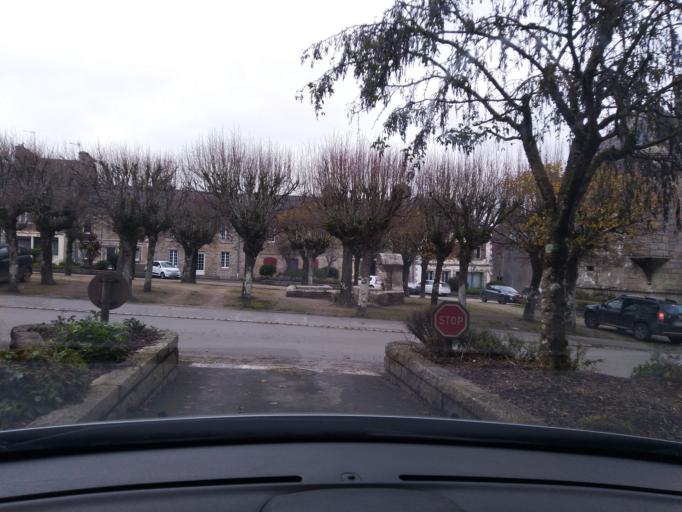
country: FR
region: Brittany
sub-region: Departement du Finistere
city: Guerlesquin
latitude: 48.5170
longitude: -3.5895
